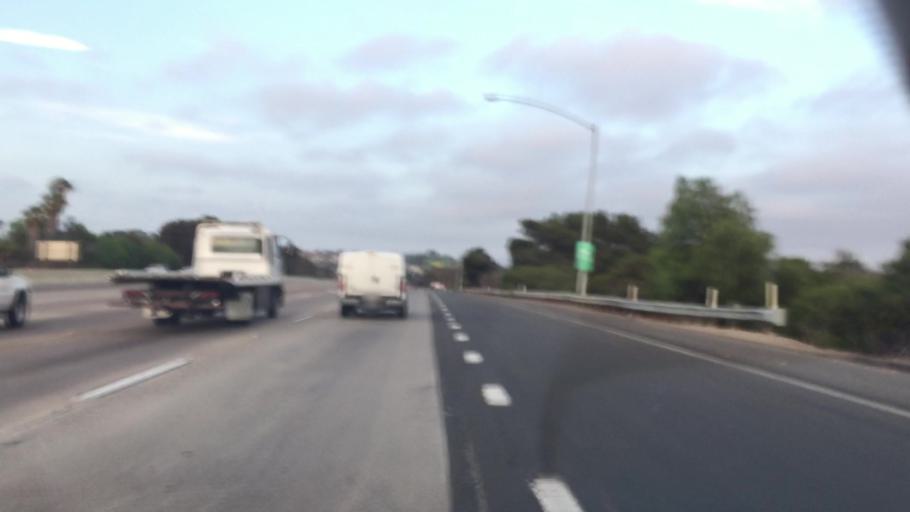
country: US
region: California
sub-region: San Diego County
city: National City
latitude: 32.7177
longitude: -117.0910
